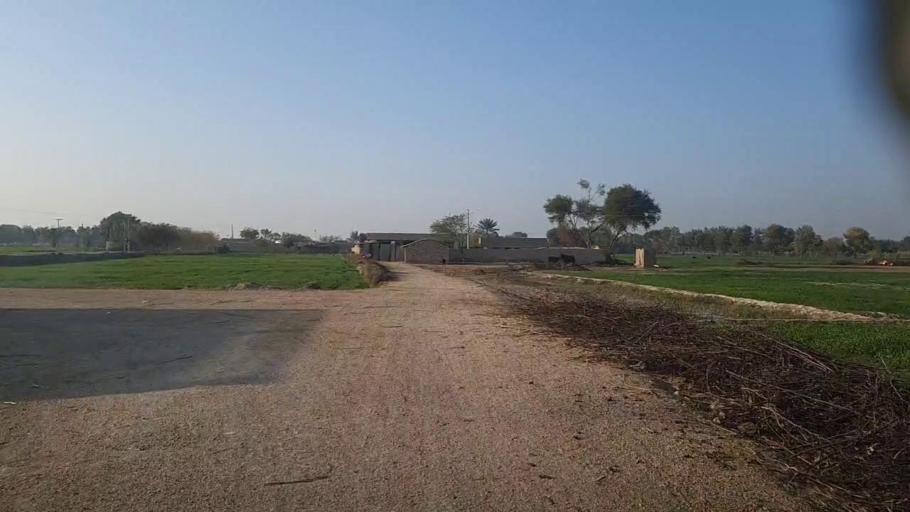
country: PK
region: Sindh
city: Khairpur
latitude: 28.0756
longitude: 69.7343
